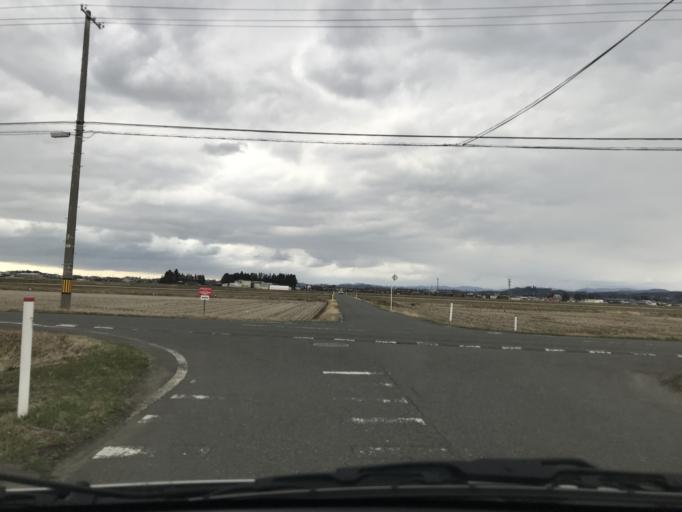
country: JP
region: Iwate
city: Mizusawa
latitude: 39.1063
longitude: 141.1631
